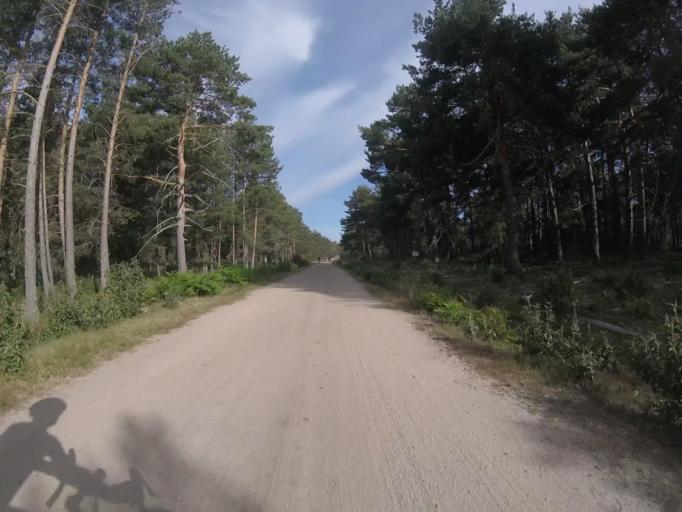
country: ES
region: Castille and Leon
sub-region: Provincia de Avila
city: Peguerinos
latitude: 40.6517
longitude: -4.1798
